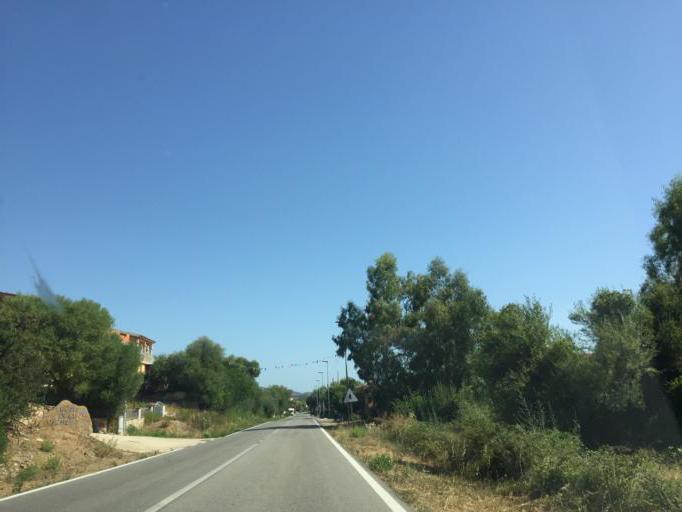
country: IT
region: Sardinia
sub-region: Provincia di Olbia-Tempio
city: San Teodoro
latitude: 40.7409
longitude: 9.6462
